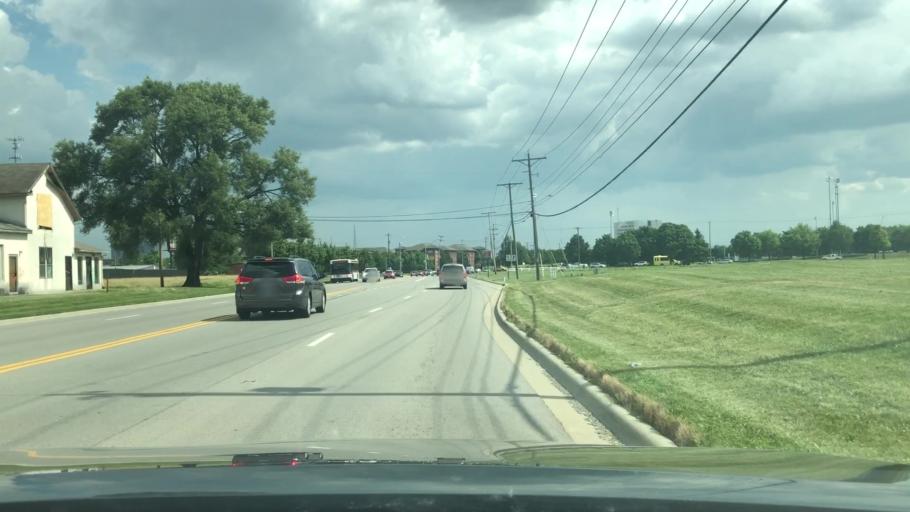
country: US
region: Ohio
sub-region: Franklin County
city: Grandview Heights
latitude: 40.0090
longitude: -83.0353
